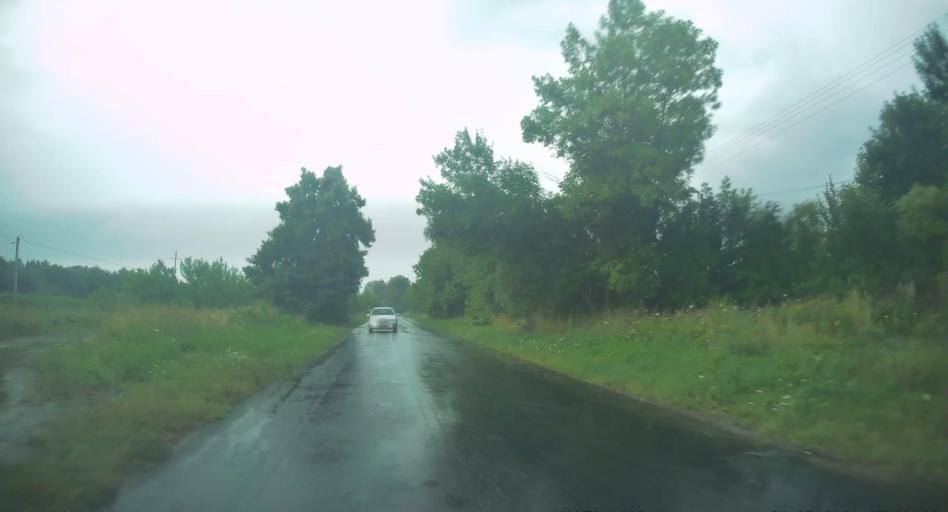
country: PL
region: Lodz Voivodeship
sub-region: Powiat brzezinski
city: Rogow
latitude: 51.8105
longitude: 19.8763
